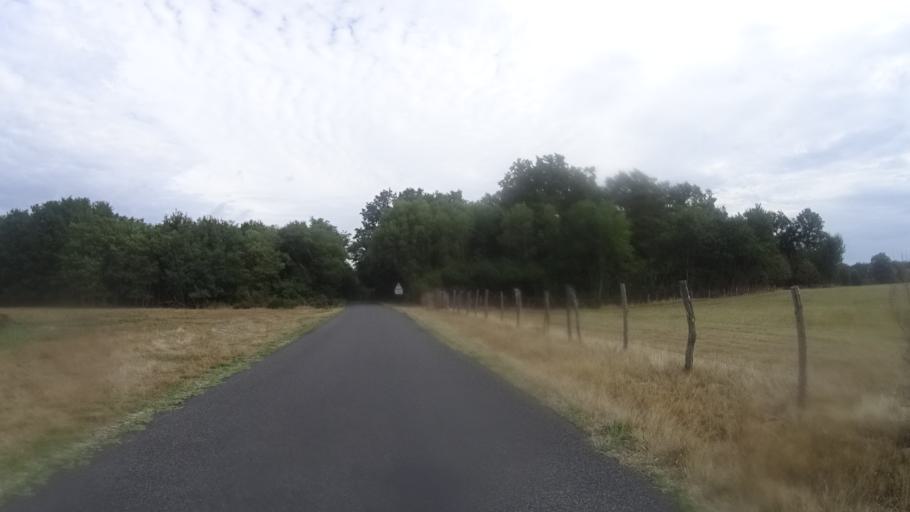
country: FR
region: Centre
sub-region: Departement du Loiret
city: Fay-aux-Loges
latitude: 47.9661
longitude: 2.1836
